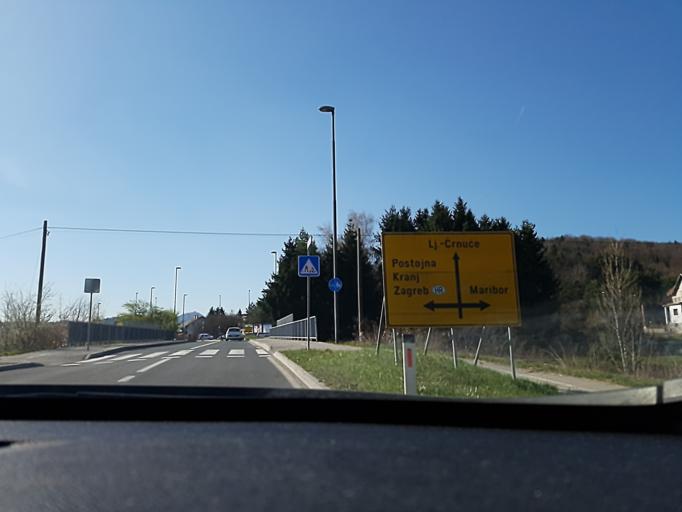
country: SI
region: Trzin
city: Trzin
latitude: 46.1040
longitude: 14.5455
